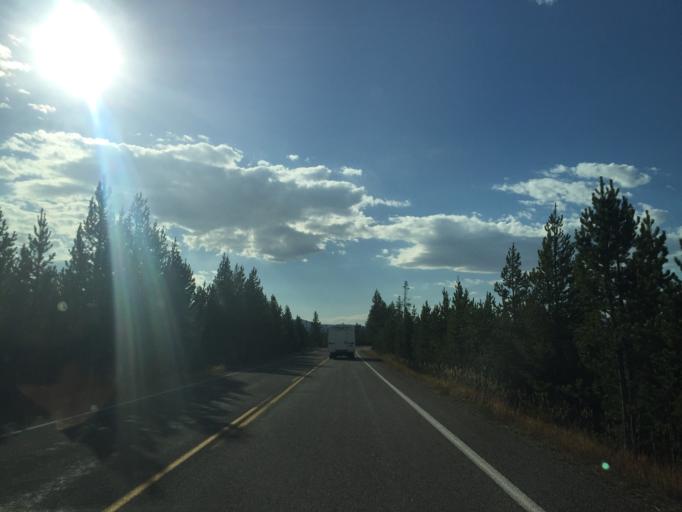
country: US
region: Montana
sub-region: Gallatin County
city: West Yellowstone
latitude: 44.6499
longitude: -111.0162
